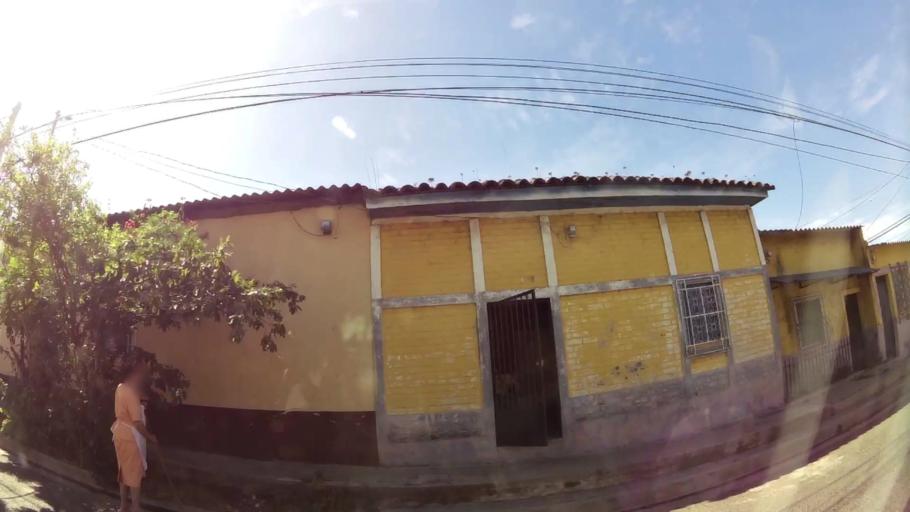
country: SV
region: Santa Ana
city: Chalchuapa
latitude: 13.9841
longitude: -89.6817
